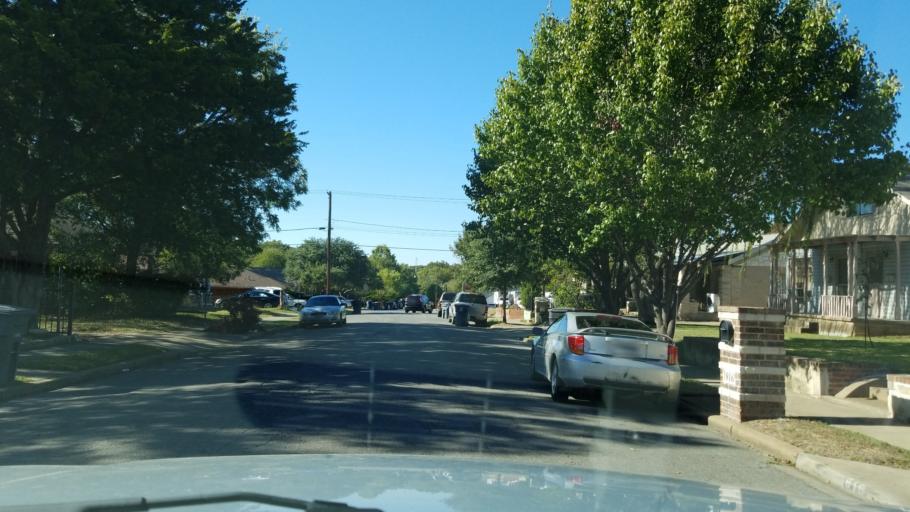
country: US
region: Texas
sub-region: Dallas County
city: Highland Park
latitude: 32.7989
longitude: -96.7470
